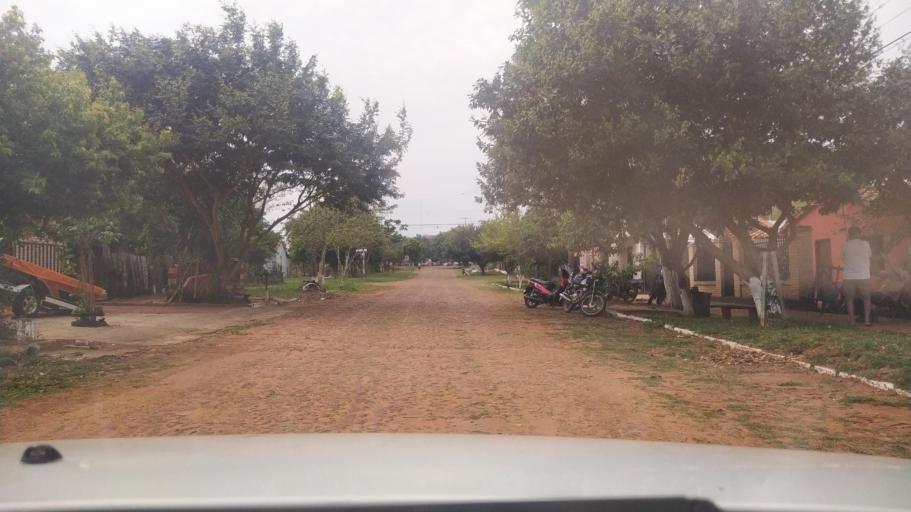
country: PY
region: Misiones
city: San Juan Bautista
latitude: -26.6725
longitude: -57.1531
